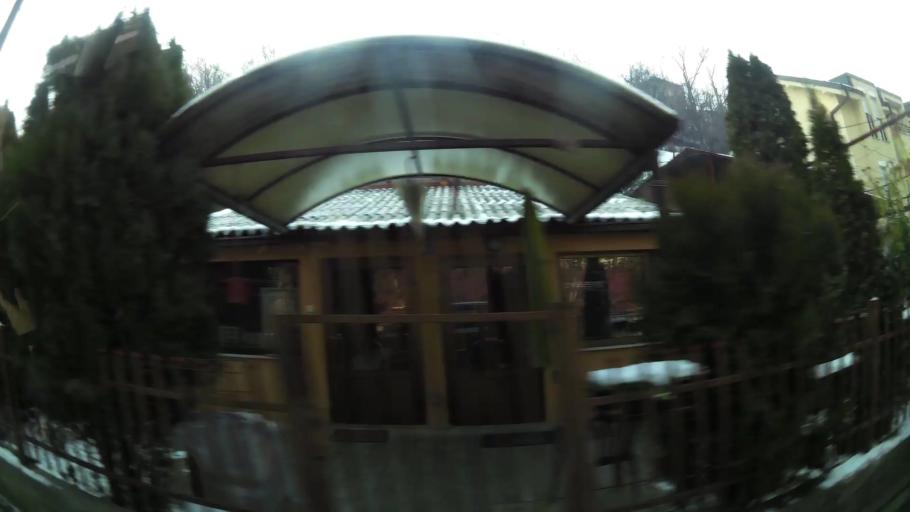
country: MK
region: Karpos
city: Skopje
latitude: 41.9872
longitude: 21.4230
